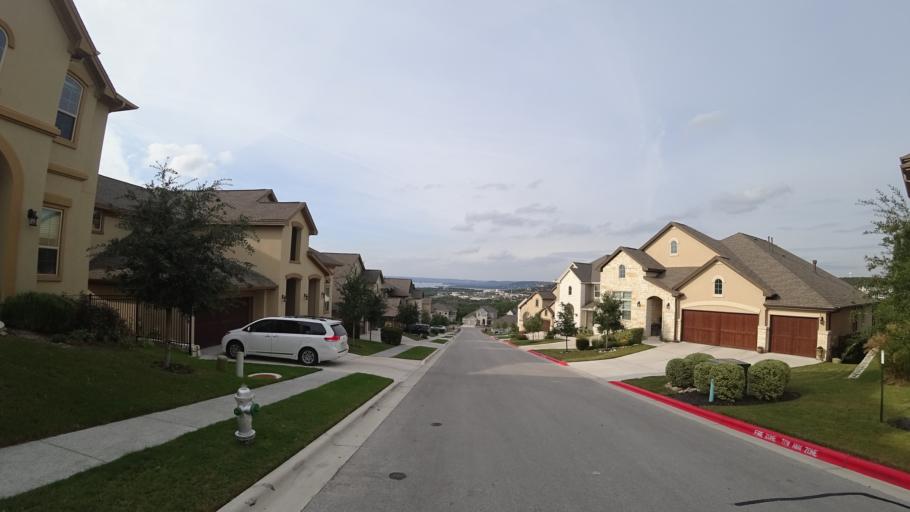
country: US
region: Texas
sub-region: Travis County
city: Hudson Bend
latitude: 30.3790
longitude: -97.8804
